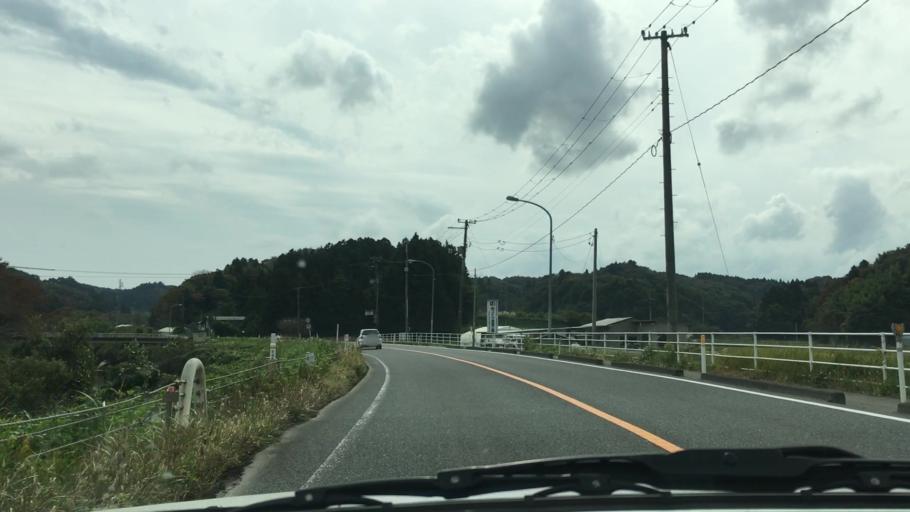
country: JP
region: Miyagi
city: Matsushima
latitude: 38.4310
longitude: 141.0609
